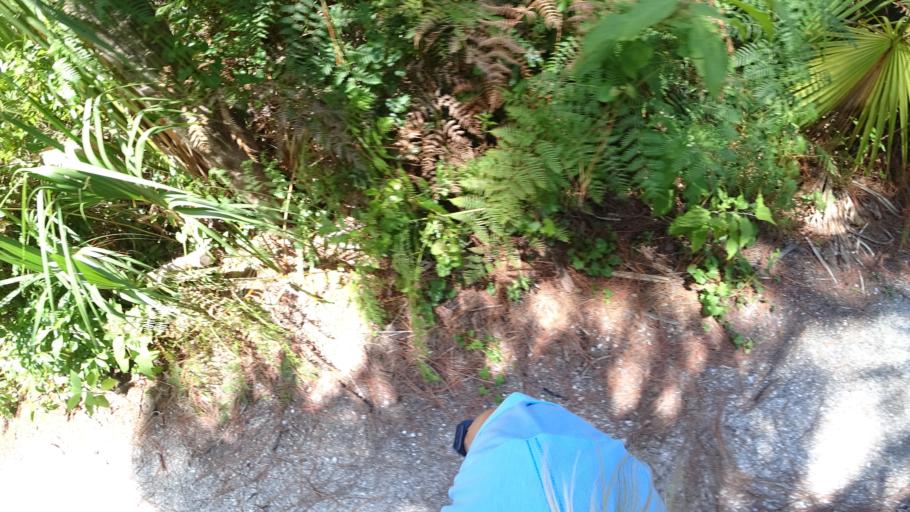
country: US
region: Florida
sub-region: Manatee County
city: West Bradenton
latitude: 27.5211
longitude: -82.6433
